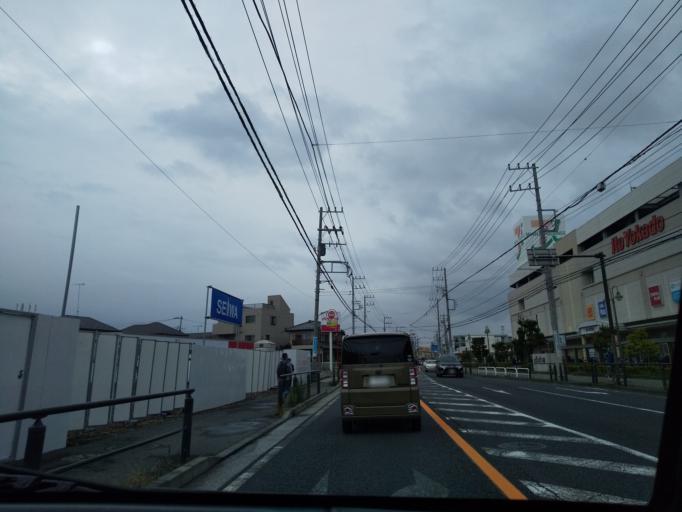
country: JP
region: Kanagawa
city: Fujisawa
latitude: 35.4125
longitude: 139.4998
